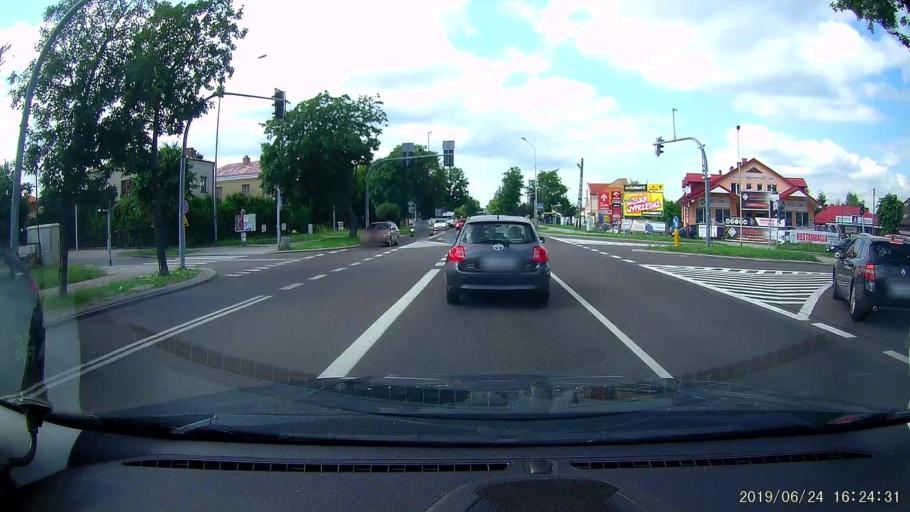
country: PL
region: Lublin Voivodeship
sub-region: Powiat tomaszowski
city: Tomaszow Lubelski
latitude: 50.4362
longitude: 23.4200
